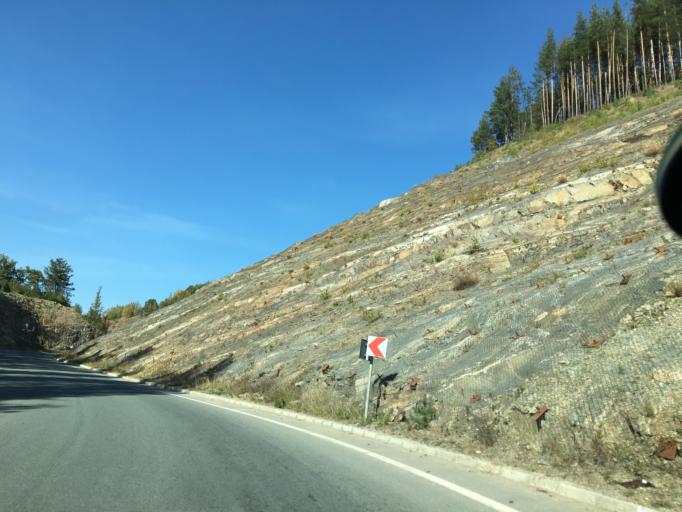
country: BG
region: Smolyan
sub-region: Obshtina Devin
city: Devin
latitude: 41.7450
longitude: 24.4342
